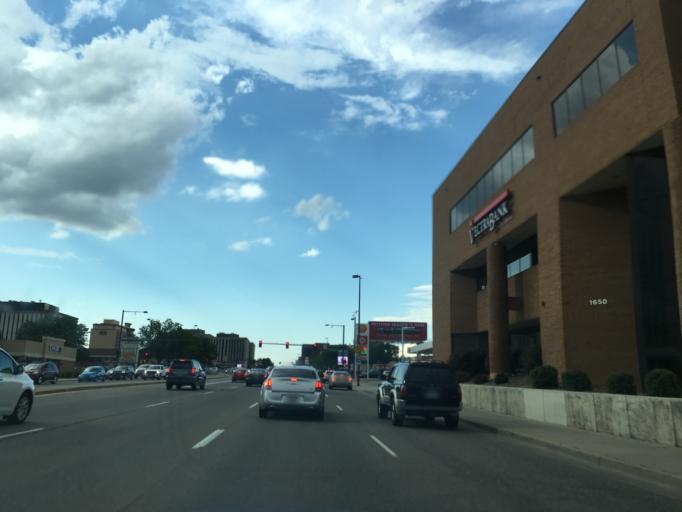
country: US
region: Colorado
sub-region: Arapahoe County
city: Glendale
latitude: 39.6864
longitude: -104.9406
